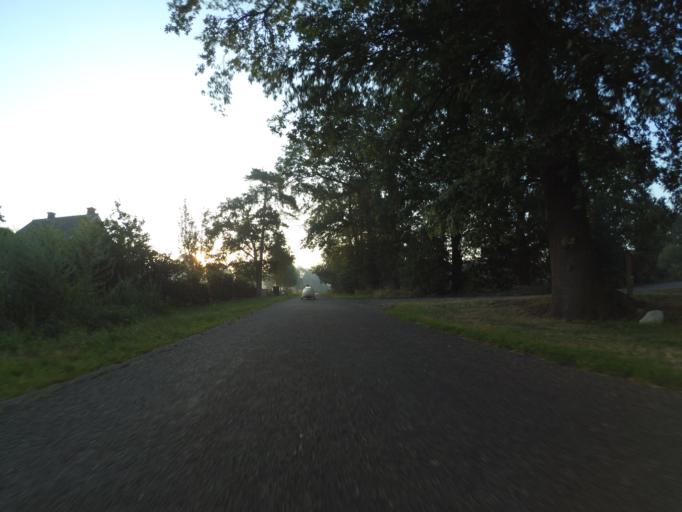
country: NL
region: Overijssel
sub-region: Gemeente Tubbergen
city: Tubbergen
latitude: 52.3955
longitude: 6.7185
